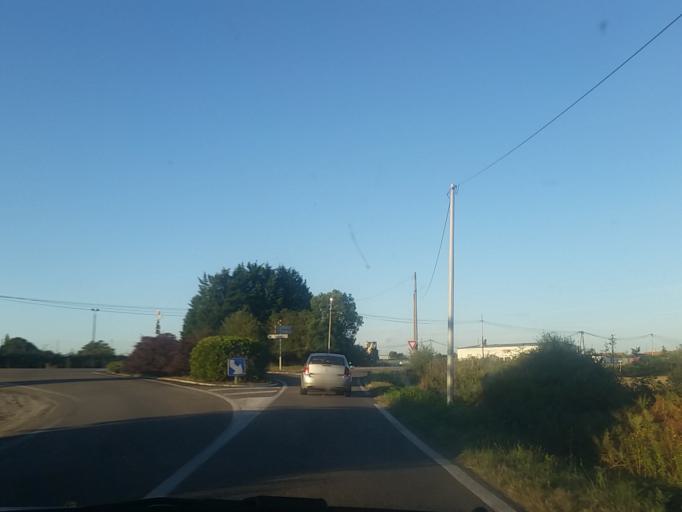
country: FR
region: Pays de la Loire
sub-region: Departement de la Loire-Atlantique
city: Vue
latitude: 47.2001
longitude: -1.9024
